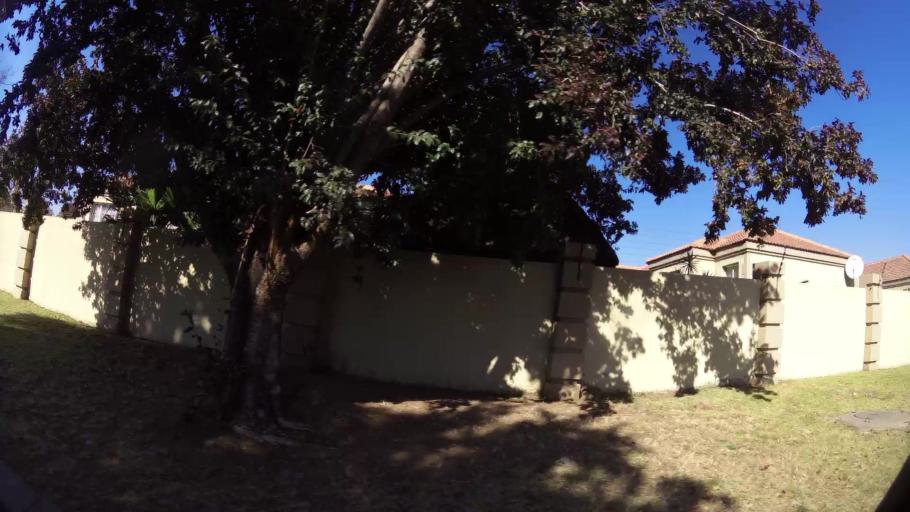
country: ZA
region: Gauteng
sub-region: Ekurhuleni Metropolitan Municipality
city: Germiston
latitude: -26.2413
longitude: 28.1077
